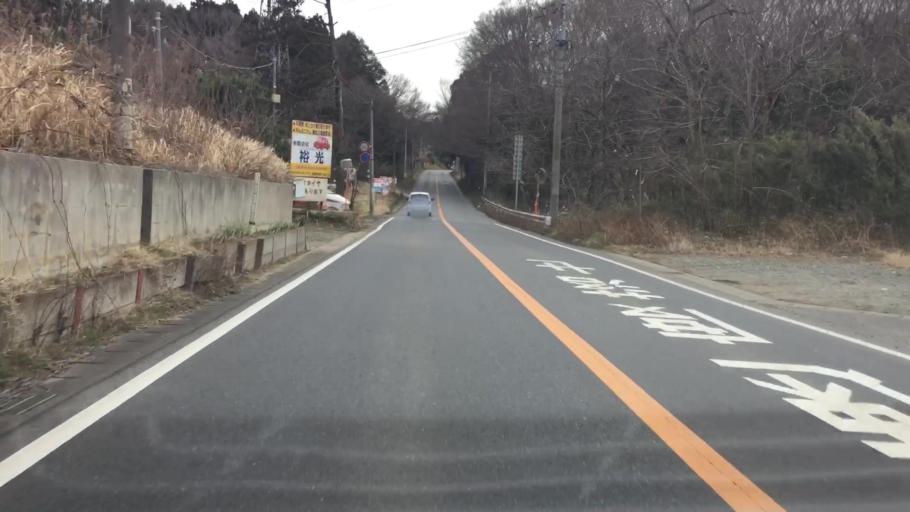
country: JP
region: Ibaraki
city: Ryugasaki
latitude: 35.8228
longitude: 140.1700
